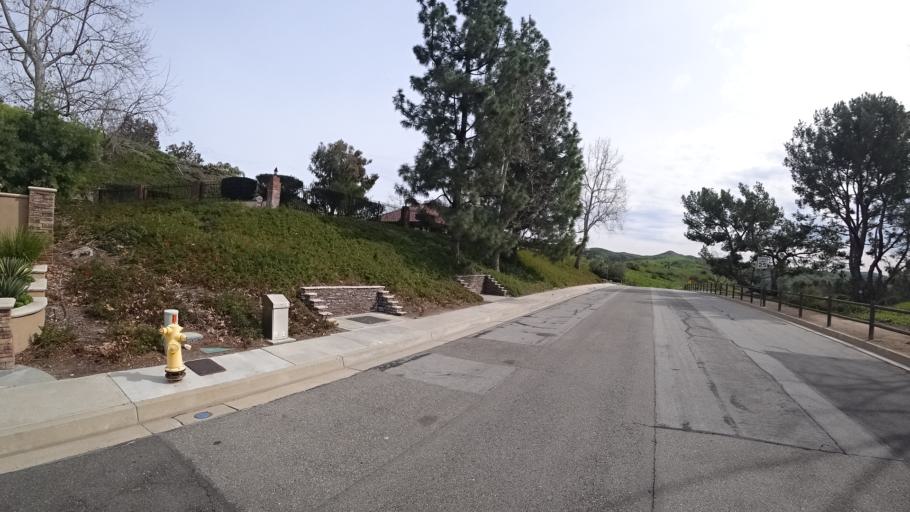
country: US
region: California
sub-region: Orange County
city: Villa Park
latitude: 33.8338
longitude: -117.7451
